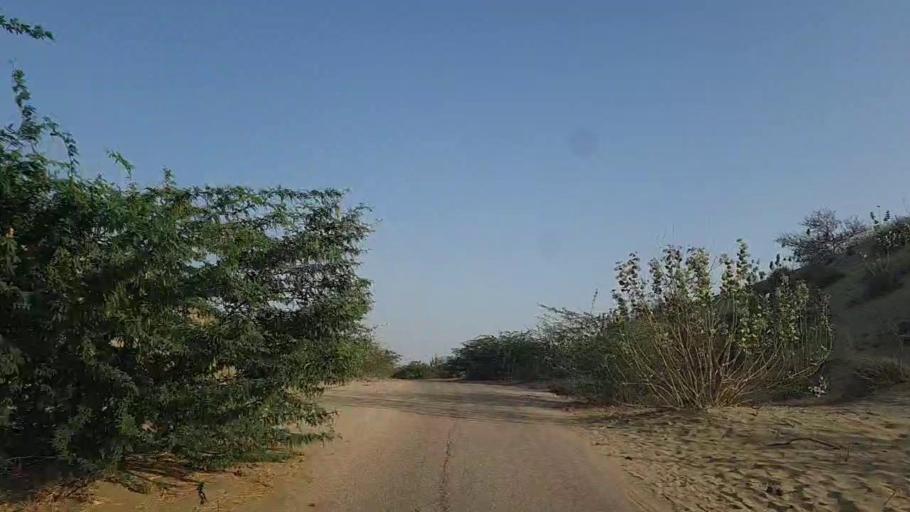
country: PK
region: Sindh
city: Diplo
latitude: 24.6003
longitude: 69.3820
